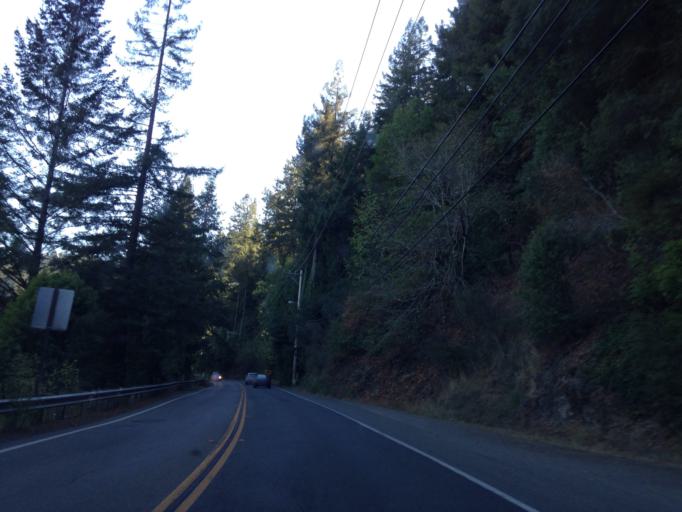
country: US
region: California
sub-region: Sonoma County
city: Guerneville
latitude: 38.4905
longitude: -123.0165
